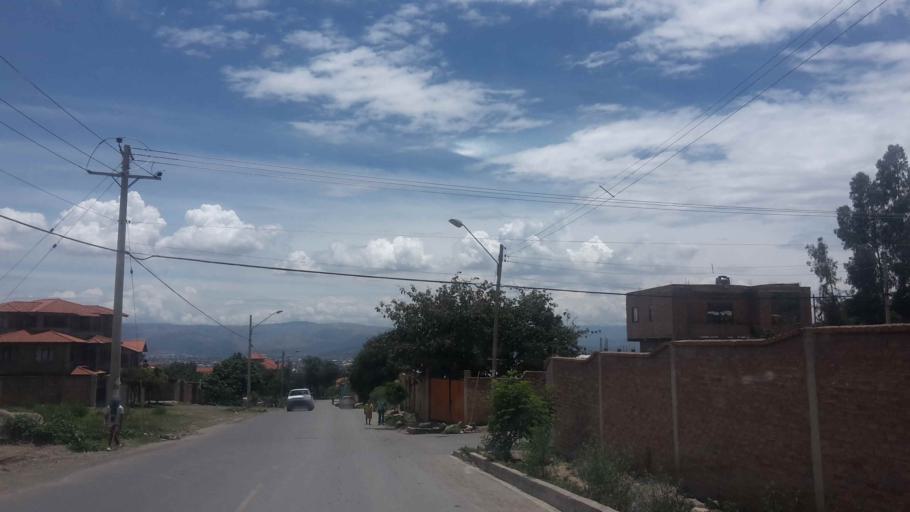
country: BO
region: Cochabamba
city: Cochabamba
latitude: -17.3451
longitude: -66.1784
